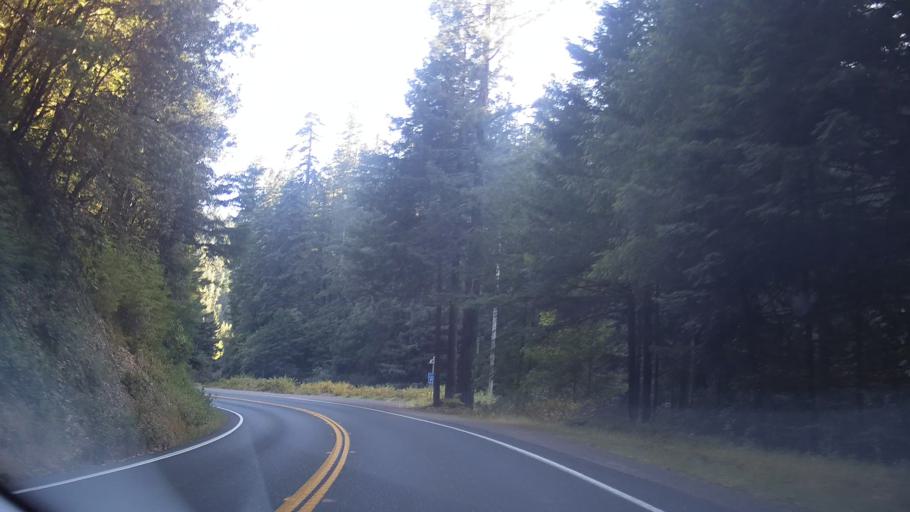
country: US
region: California
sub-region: Mendocino County
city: Brooktrails
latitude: 39.3522
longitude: -123.5105
